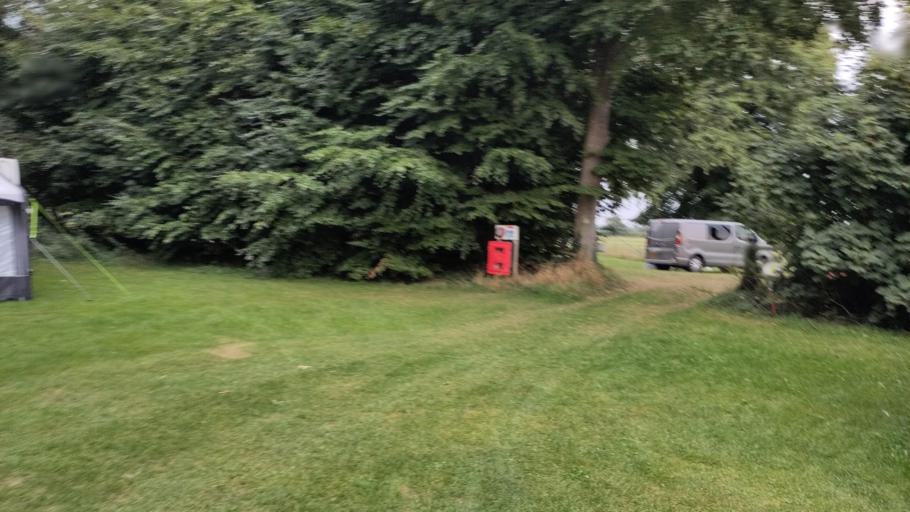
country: GB
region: England
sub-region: Cheshire West and Chester
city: Blacon
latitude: 53.1938
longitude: -2.9440
